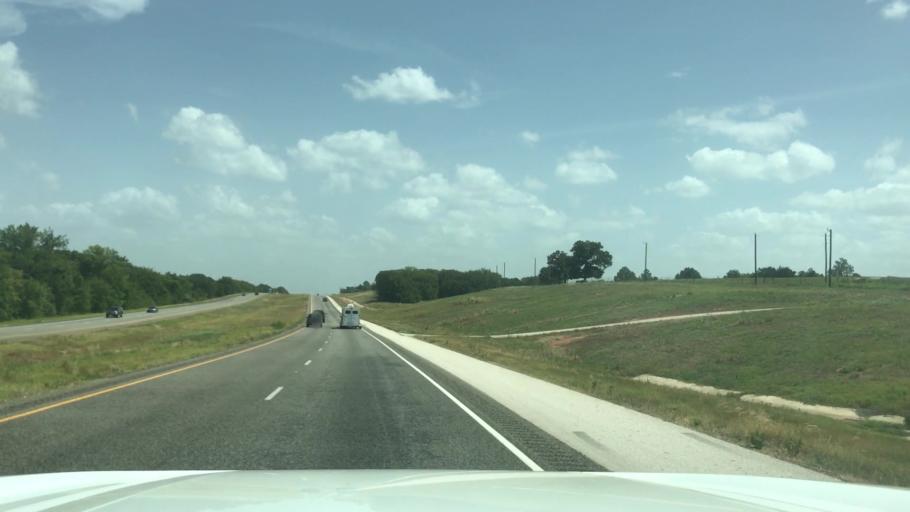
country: US
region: Texas
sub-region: Robertson County
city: Calvert
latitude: 30.9339
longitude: -96.6369
